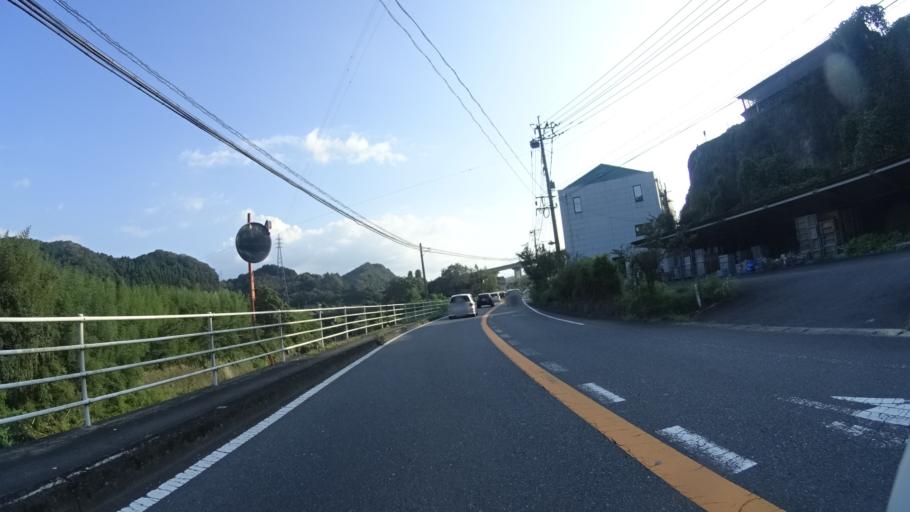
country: JP
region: Oita
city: Bungo-Takada-shi
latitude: 33.4806
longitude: 131.3349
